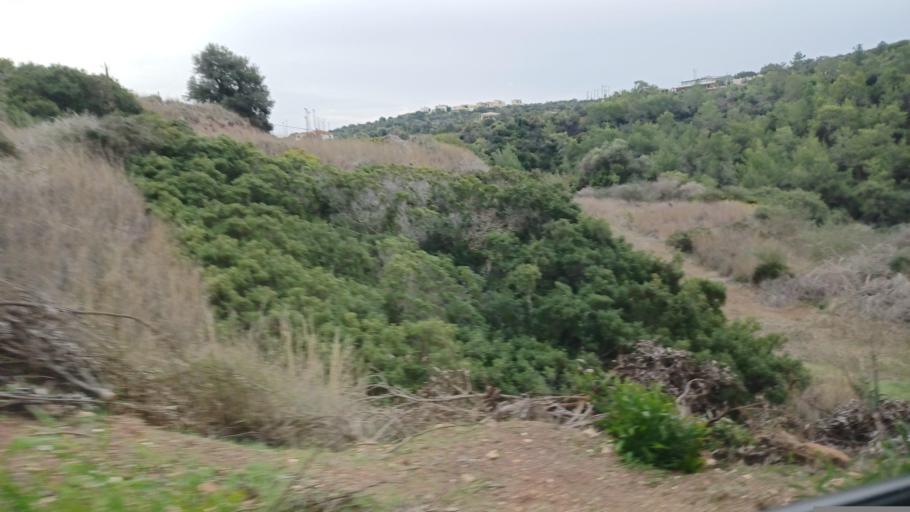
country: CY
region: Pafos
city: Polis
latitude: 35.0373
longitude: 32.3659
